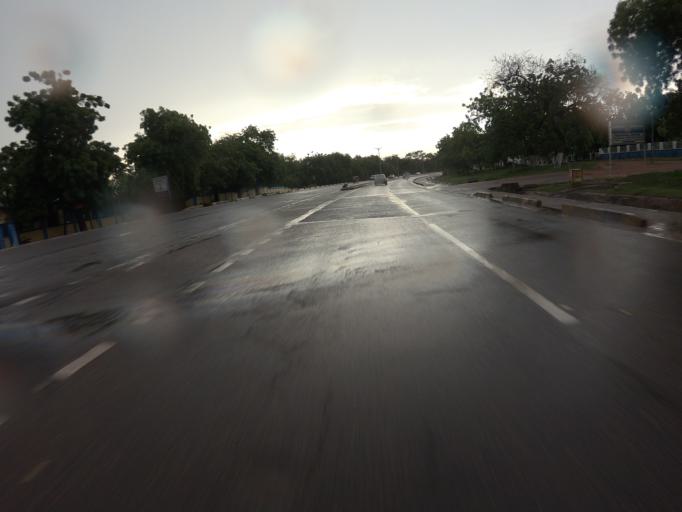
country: GH
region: Upper East
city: Bolgatanga
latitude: 10.8018
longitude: -0.8626
